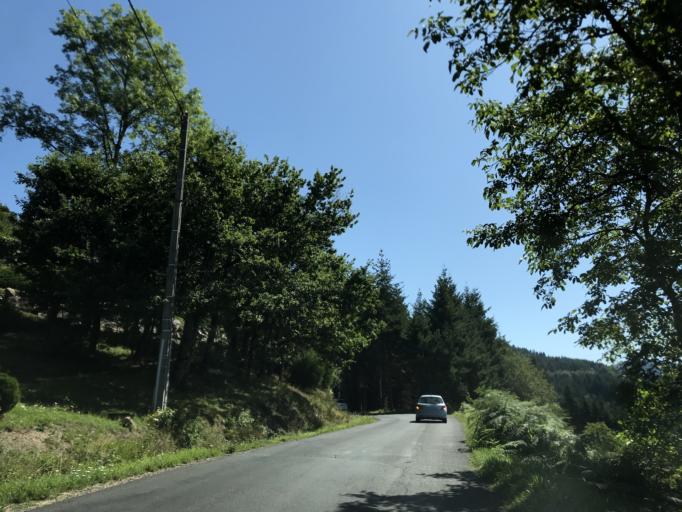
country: FR
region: Auvergne
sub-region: Departement du Puy-de-Dome
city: Job
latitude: 45.6625
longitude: 3.7155
